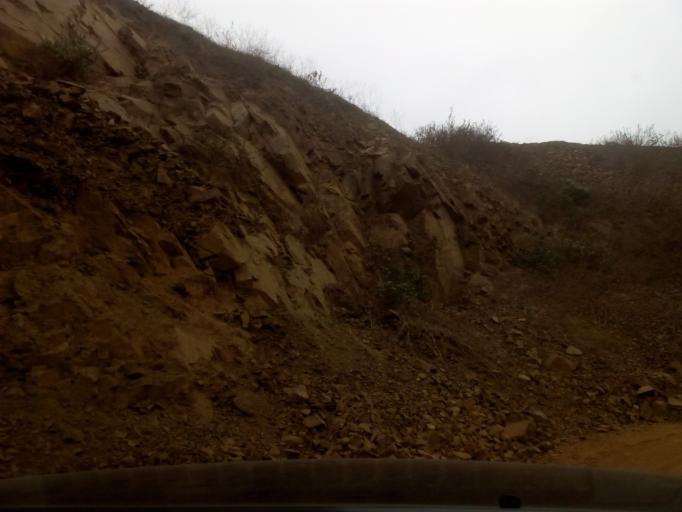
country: PE
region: La Libertad
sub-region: Viru
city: Viru
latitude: -8.3632
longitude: -78.6440
